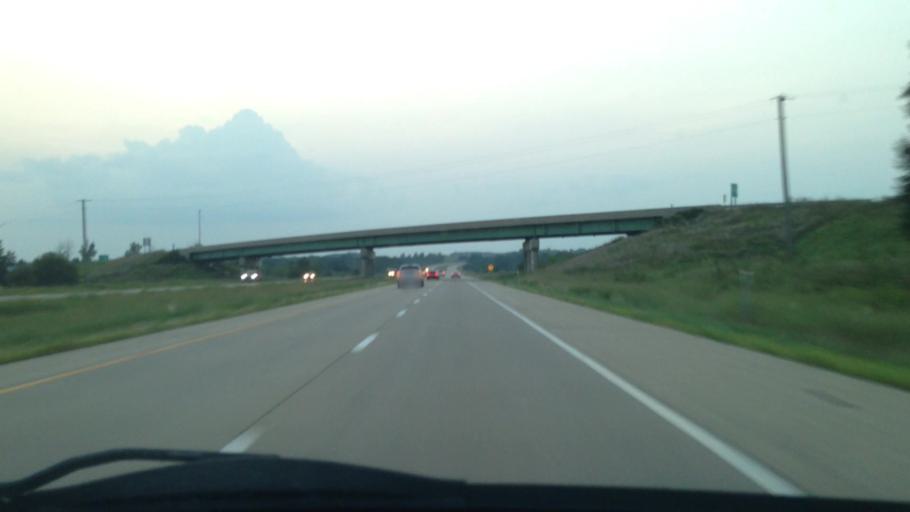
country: US
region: Iowa
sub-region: Black Hawk County
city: La Porte City
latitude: 42.4126
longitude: -92.1704
